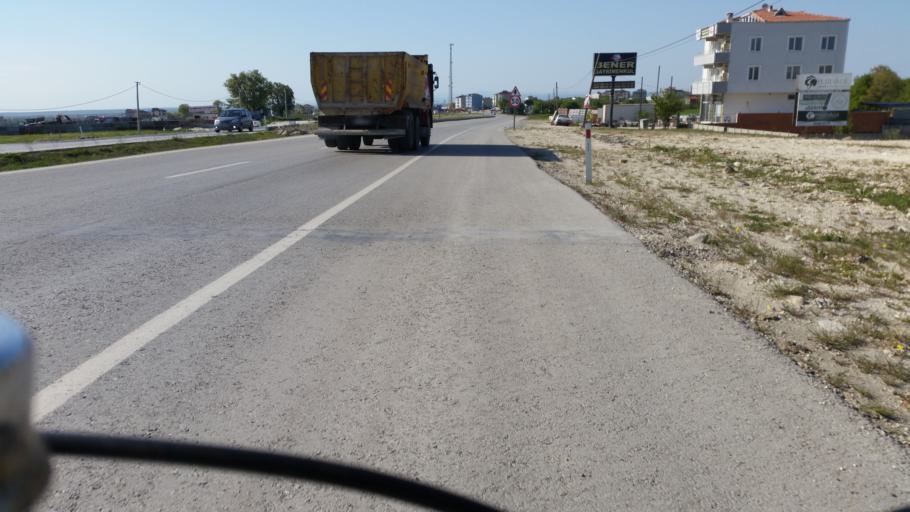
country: TR
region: Tekirdag
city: Cerkezkoey
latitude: 41.3508
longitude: 27.9577
